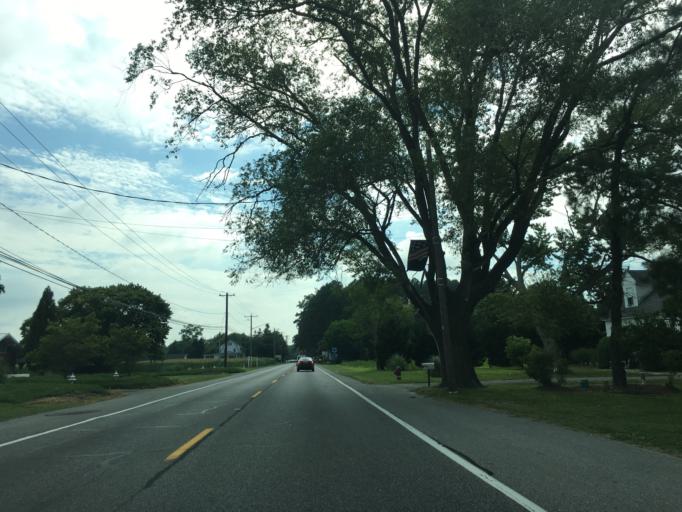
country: US
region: Delaware
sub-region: Sussex County
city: Millsboro
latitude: 38.5490
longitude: -75.2342
